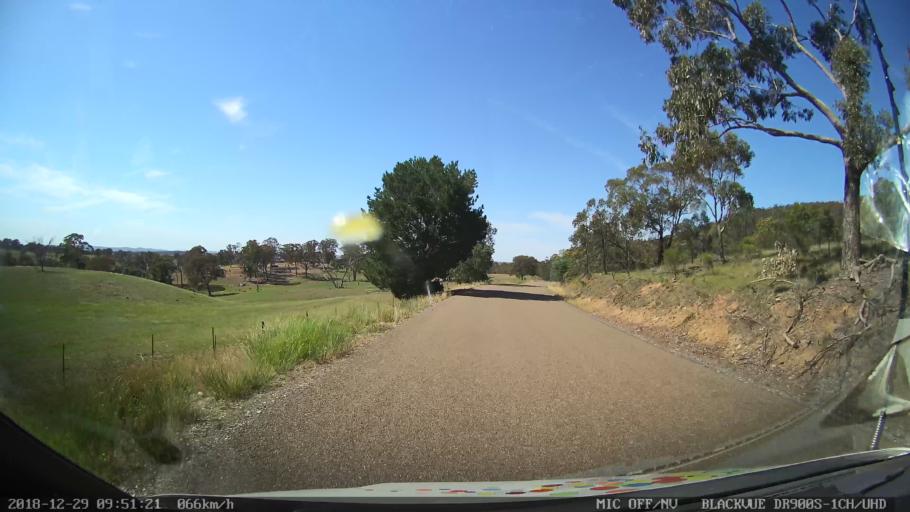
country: AU
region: New South Wales
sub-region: Goulburn Mulwaree
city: Goulburn
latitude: -34.7315
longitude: 149.4619
